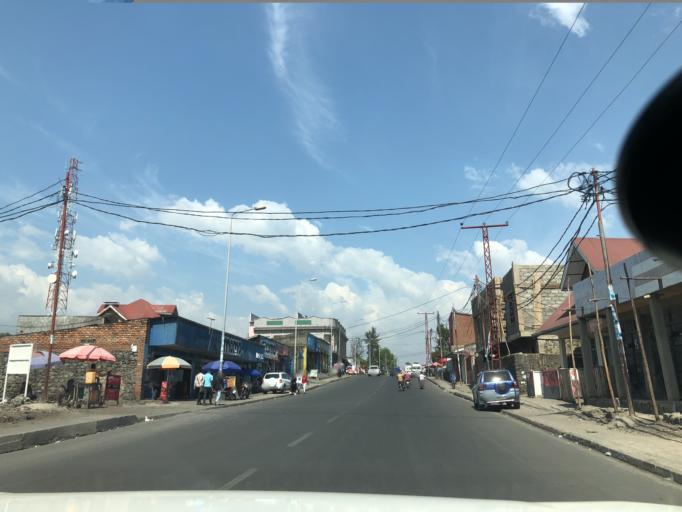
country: CD
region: Nord Kivu
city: Goma
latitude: -1.6587
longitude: 29.1895
